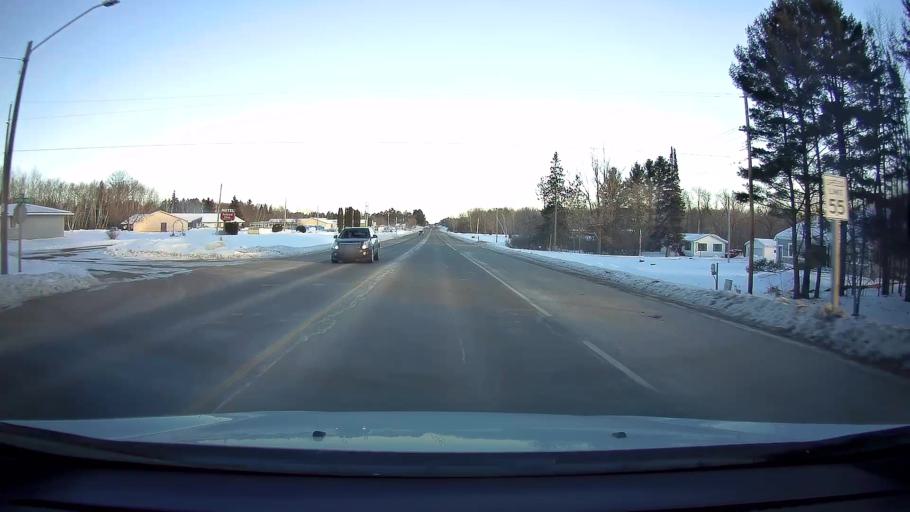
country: US
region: Wisconsin
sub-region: Barron County
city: Cumberland
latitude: 45.5496
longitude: -92.0171
